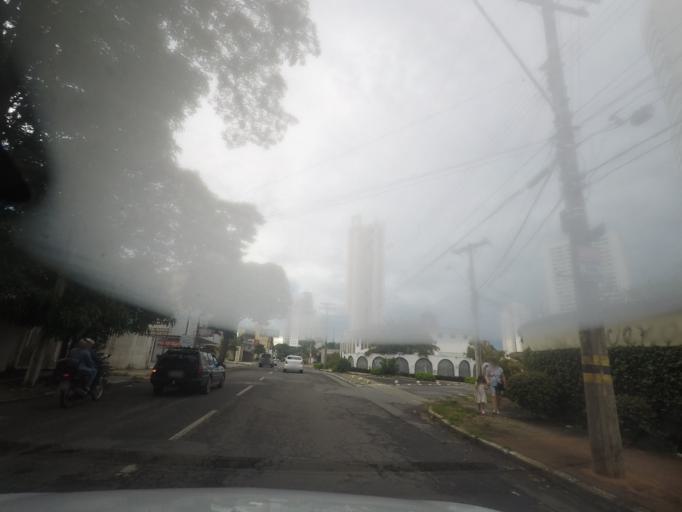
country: BR
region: Goias
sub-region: Goiania
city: Goiania
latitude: -16.6977
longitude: -49.2652
